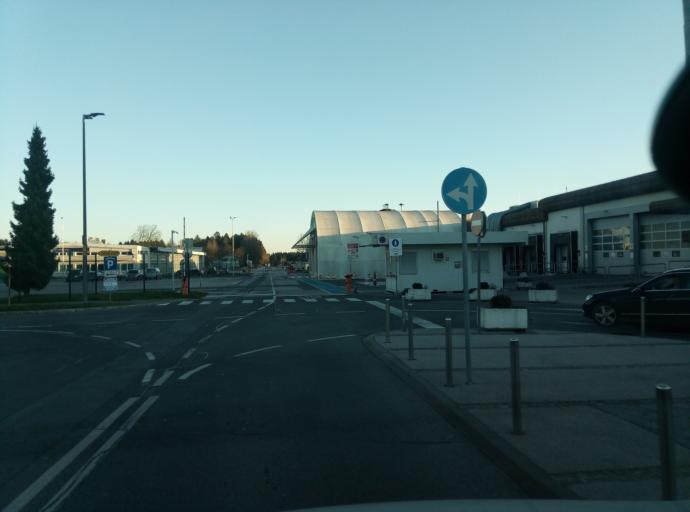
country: SI
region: Sencur
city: Sencur
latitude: 46.2308
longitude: 14.4559
